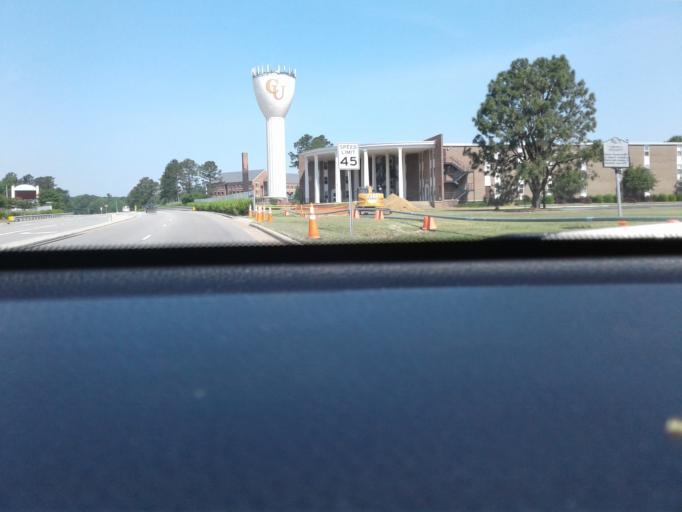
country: US
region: North Carolina
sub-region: Harnett County
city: Buies Creek
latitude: 35.4045
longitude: -78.7398
